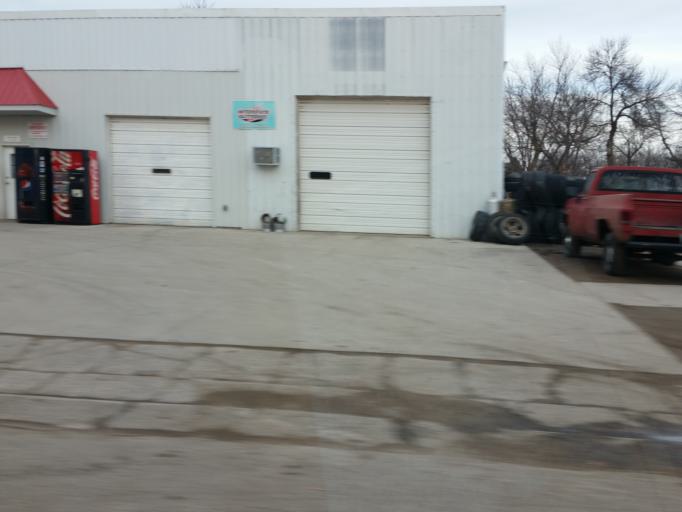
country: US
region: North Dakota
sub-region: Cass County
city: Casselton
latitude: 47.1018
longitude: -97.2181
